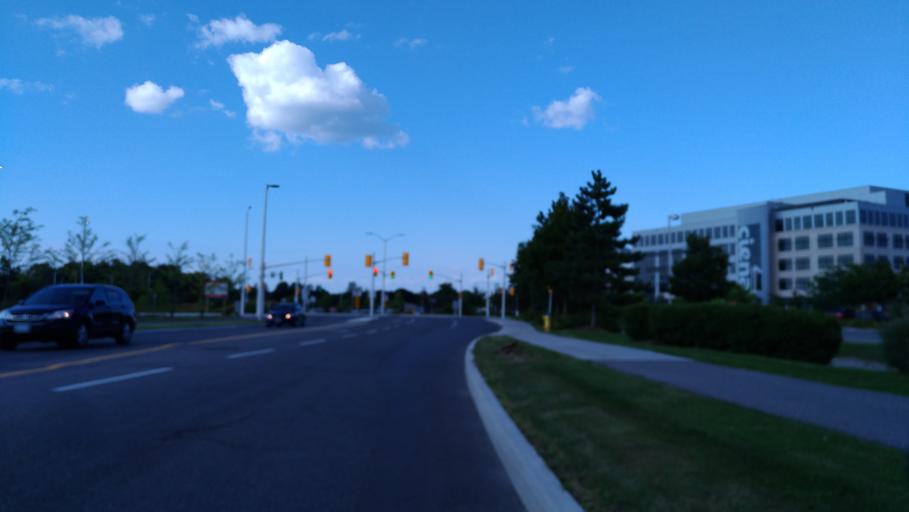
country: CA
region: Ontario
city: Bells Corners
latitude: 45.3430
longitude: -75.9303
